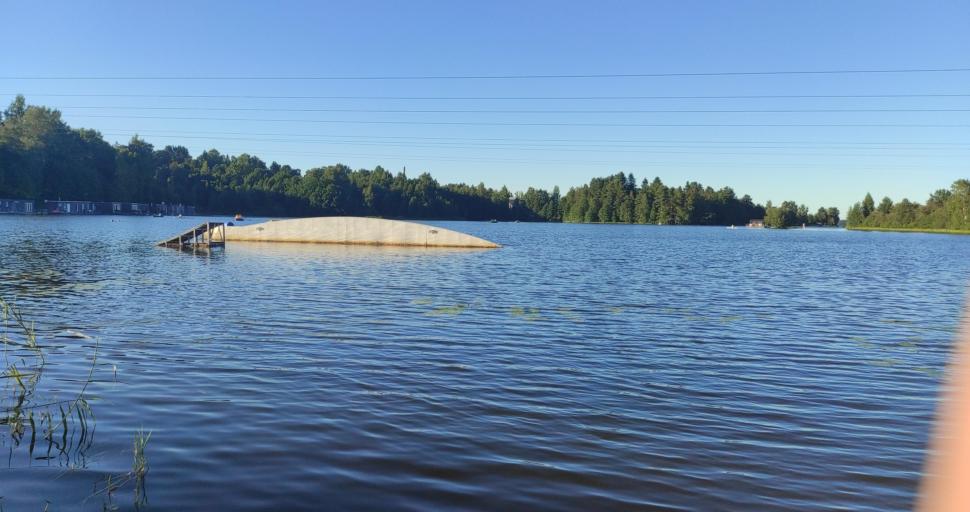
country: RU
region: Leningrad
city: Toksovo
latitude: 60.1549
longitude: 30.5557
